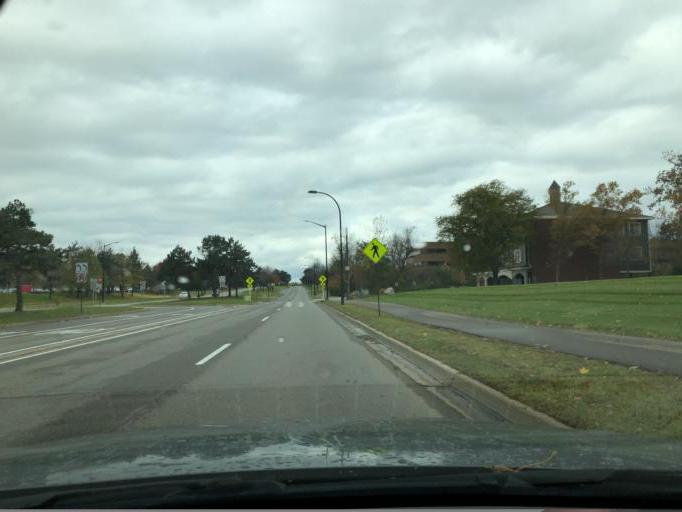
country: US
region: Michigan
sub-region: Washtenaw County
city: Ann Arbor
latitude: 42.2440
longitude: -83.7426
